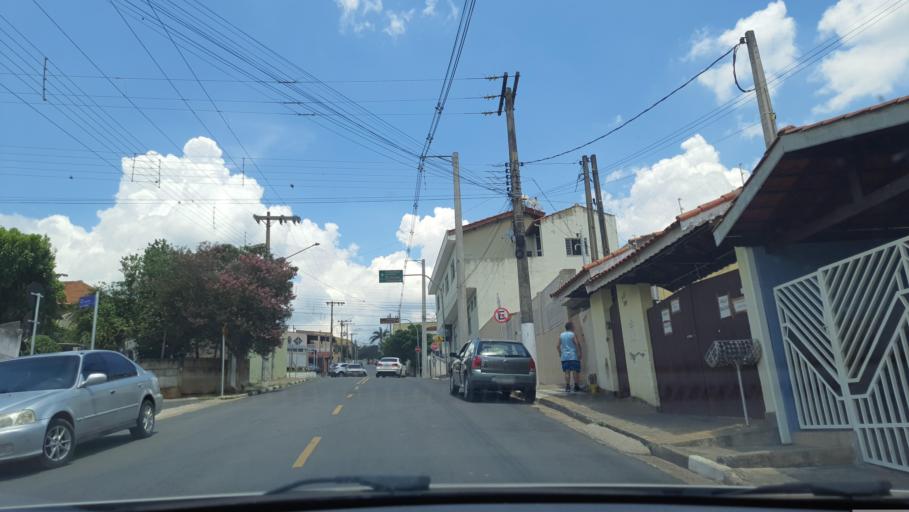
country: BR
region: Sao Paulo
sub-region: Bom Jesus Dos Perdoes
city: Bom Jesus dos Perdoes
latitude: -23.1361
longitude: -46.4665
